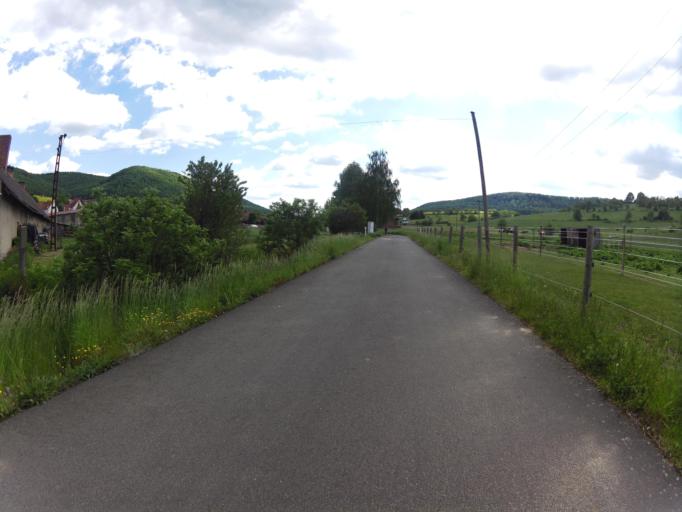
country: DE
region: Thuringia
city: Treffurt
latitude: 51.1116
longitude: 10.2209
